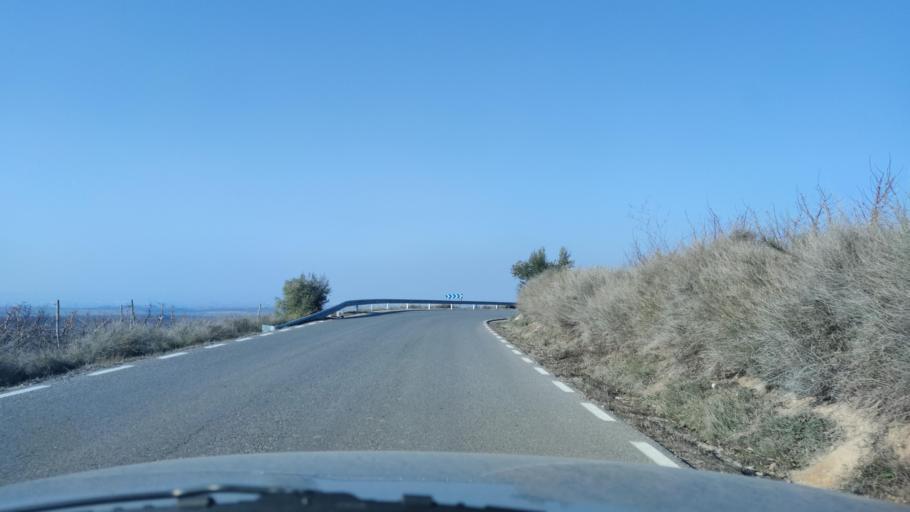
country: ES
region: Catalonia
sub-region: Provincia de Lleida
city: Sunyer
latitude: 41.5201
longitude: 0.5640
